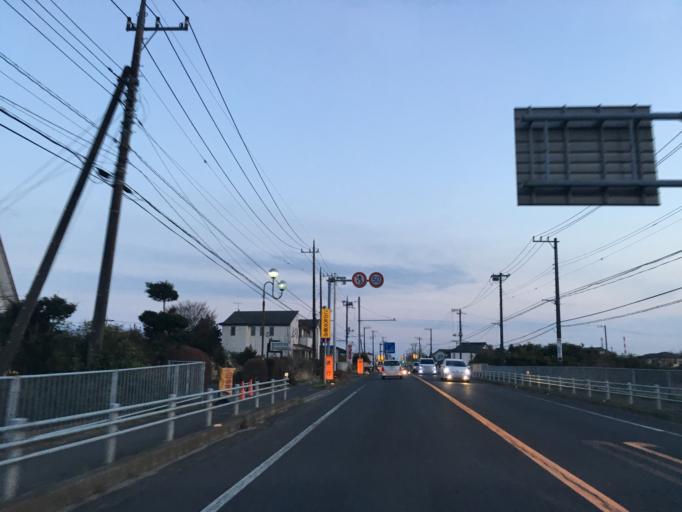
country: JP
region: Ibaraki
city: Takahagi
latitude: 36.7213
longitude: 140.7190
